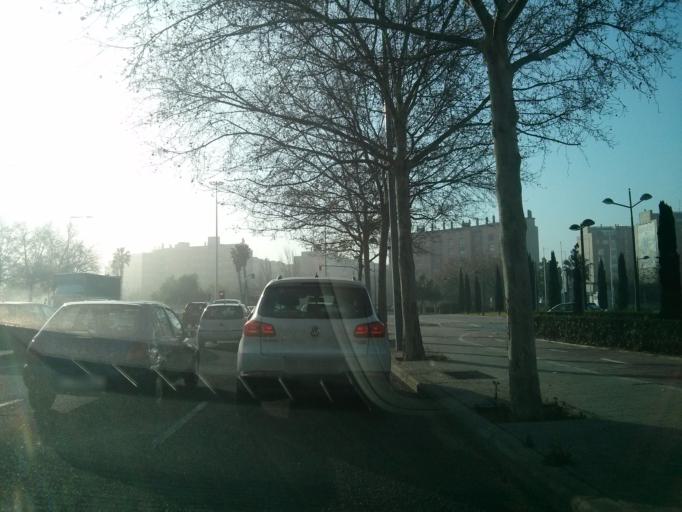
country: ES
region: Valencia
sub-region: Provincia de Valencia
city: Tavernes Blanques
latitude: 39.4985
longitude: -0.3874
